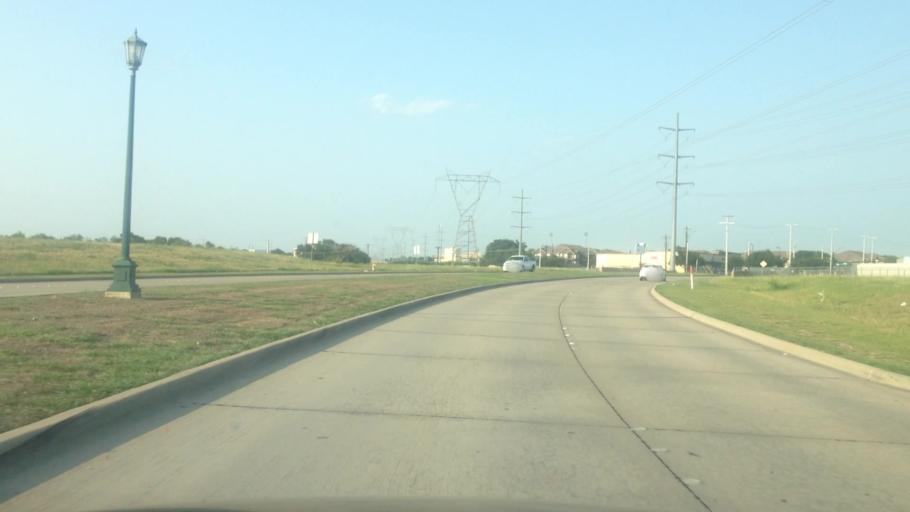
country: US
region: Texas
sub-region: Denton County
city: The Colony
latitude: 33.0669
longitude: -96.8944
